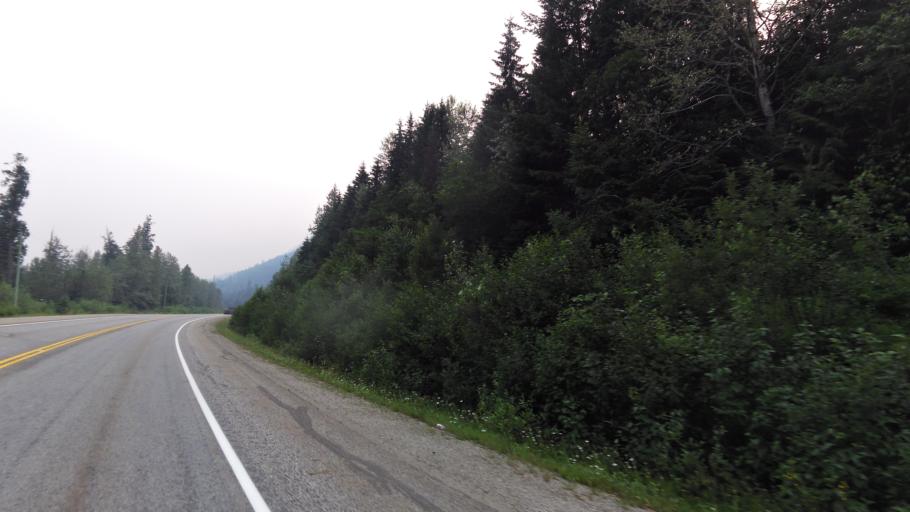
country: CA
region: Alberta
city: Jasper Park Lodge
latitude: 52.3282
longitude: -119.1767
